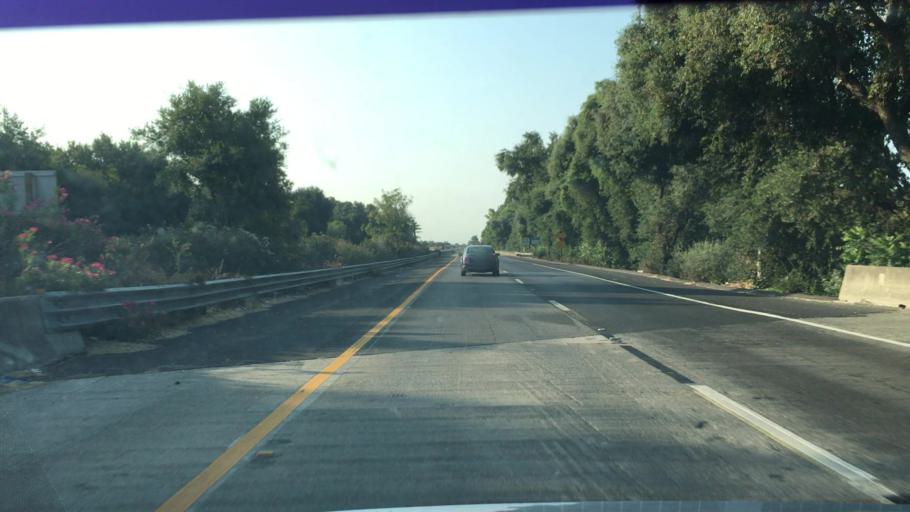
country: US
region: California
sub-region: Sacramento County
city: Galt
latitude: 38.2454
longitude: -121.2880
